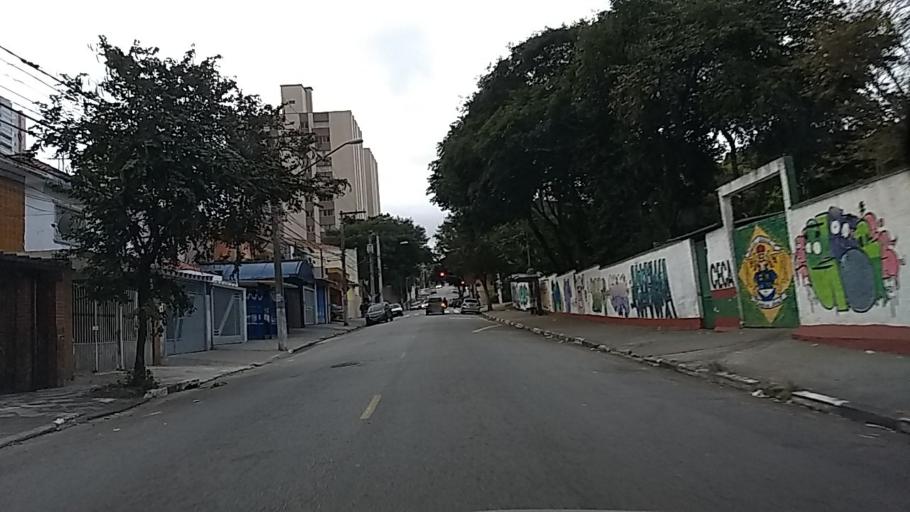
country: BR
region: Sao Paulo
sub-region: Sao Paulo
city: Sao Paulo
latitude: -23.5077
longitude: -46.6017
